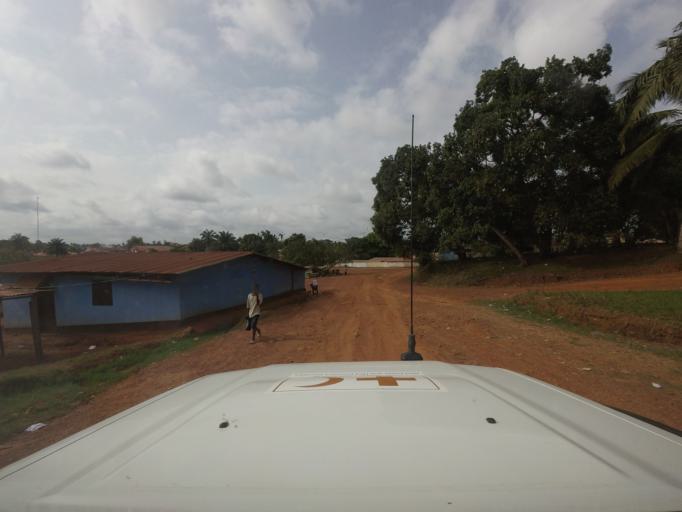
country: LR
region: Bong
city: Gbarnga
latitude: 7.0030
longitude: -9.4745
